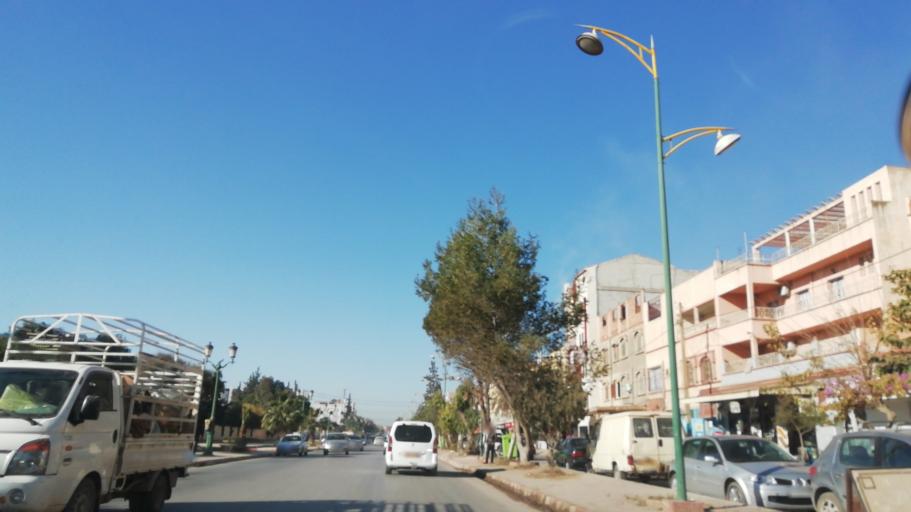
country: DZ
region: Tlemcen
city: Nedroma
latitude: 34.8454
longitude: -1.7438
